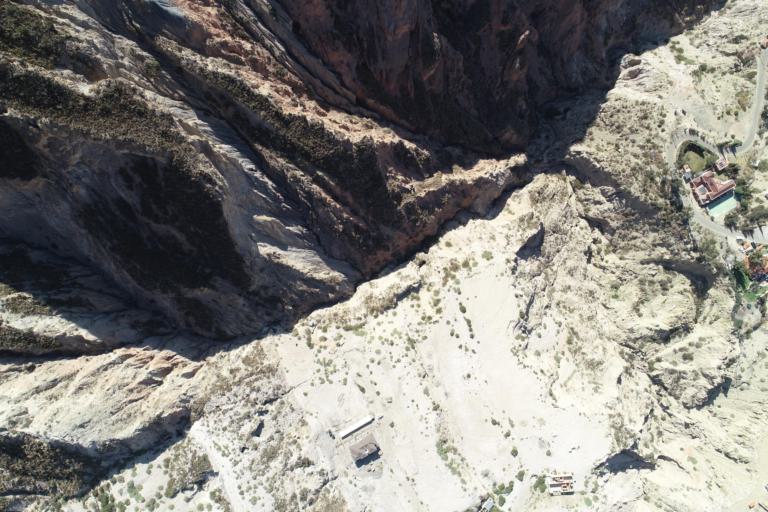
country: BO
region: La Paz
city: La Paz
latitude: -16.5552
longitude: -68.1055
